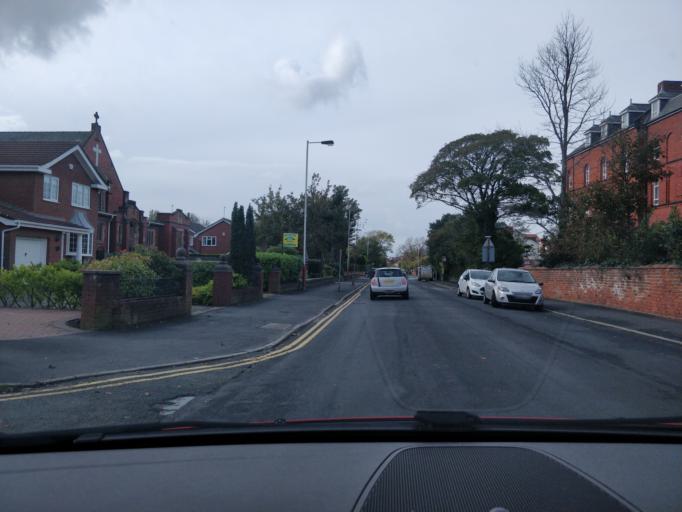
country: GB
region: England
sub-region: Sefton
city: Southport
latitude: 53.6299
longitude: -3.0199
